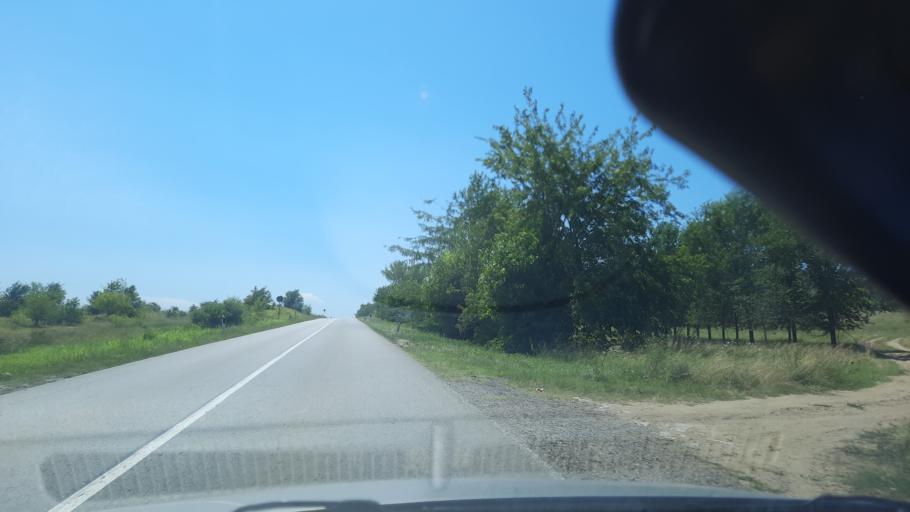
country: RO
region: Caras-Severin
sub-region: Comuna Socol
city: Socol
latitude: 44.8730
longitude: 21.3222
